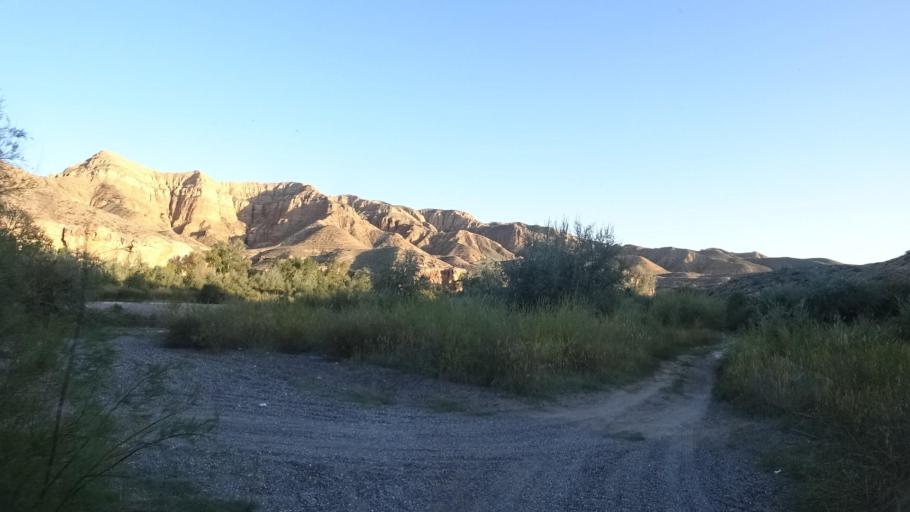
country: KZ
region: Almaty Oblysy
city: Kegen
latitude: 43.2738
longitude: 78.9771
